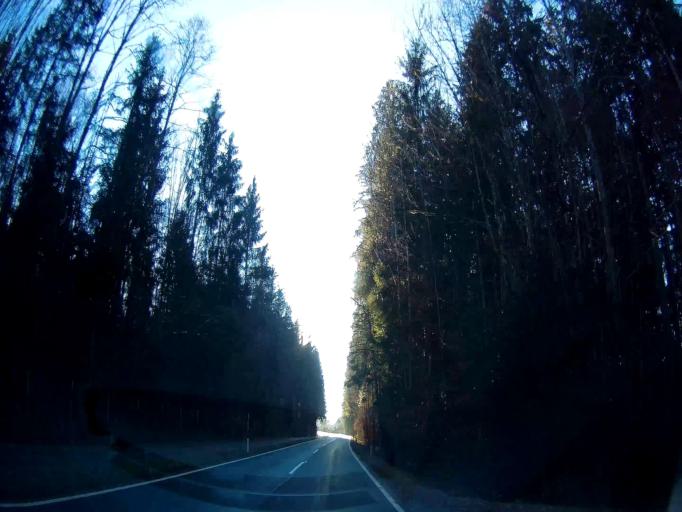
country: DE
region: Bavaria
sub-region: Upper Bavaria
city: Piding
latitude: 47.7640
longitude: 12.9497
